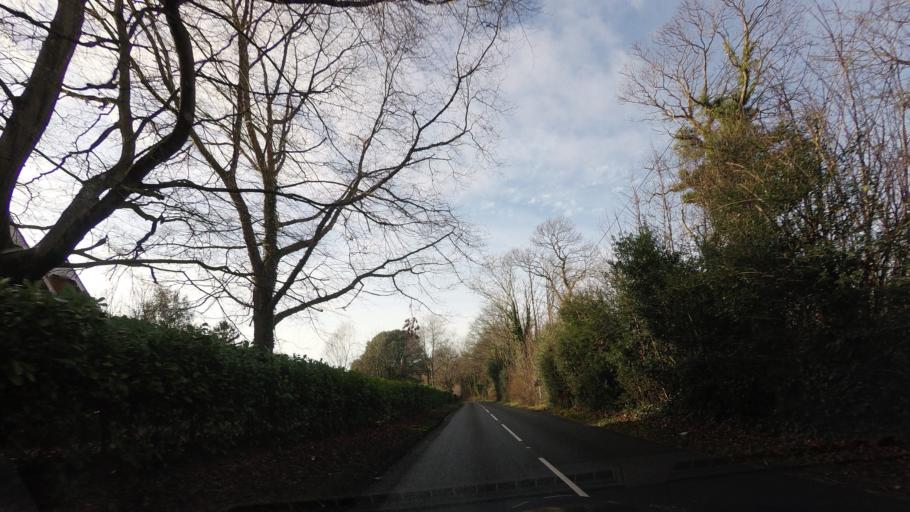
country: GB
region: England
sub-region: East Sussex
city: Battle
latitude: 50.9034
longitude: 0.4712
